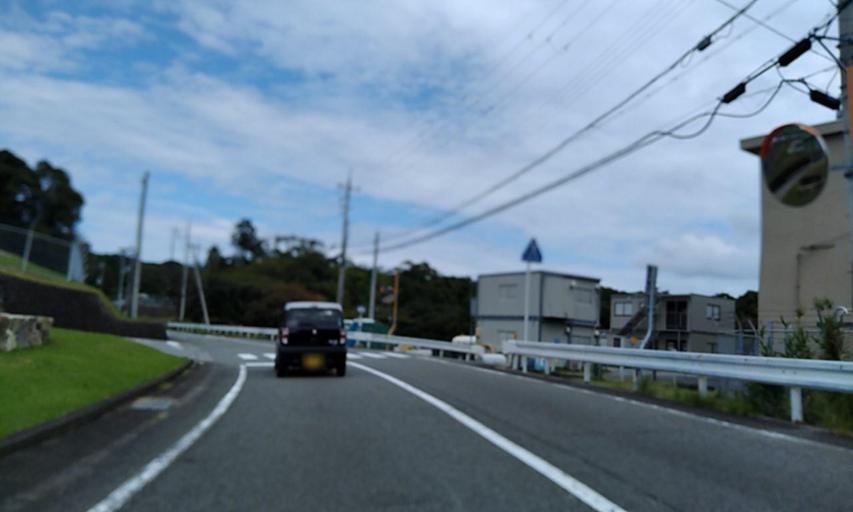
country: JP
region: Wakayama
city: Shingu
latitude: 33.4666
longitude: 135.8301
